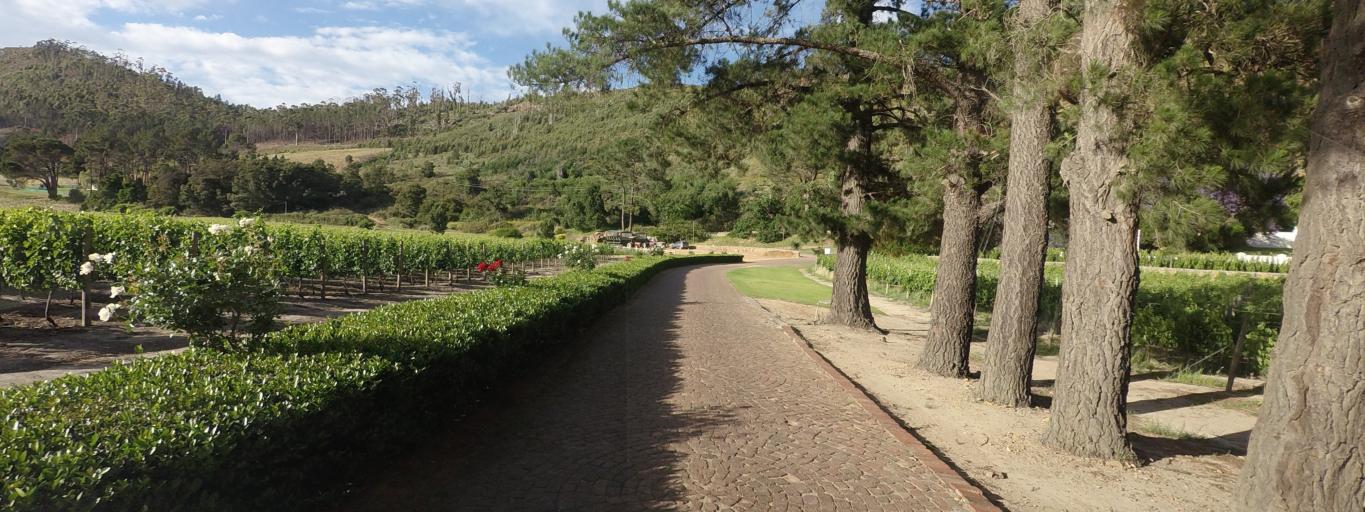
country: ZA
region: Western Cape
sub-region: Cape Winelands District Municipality
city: Paarl
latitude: -33.8997
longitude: 19.0926
